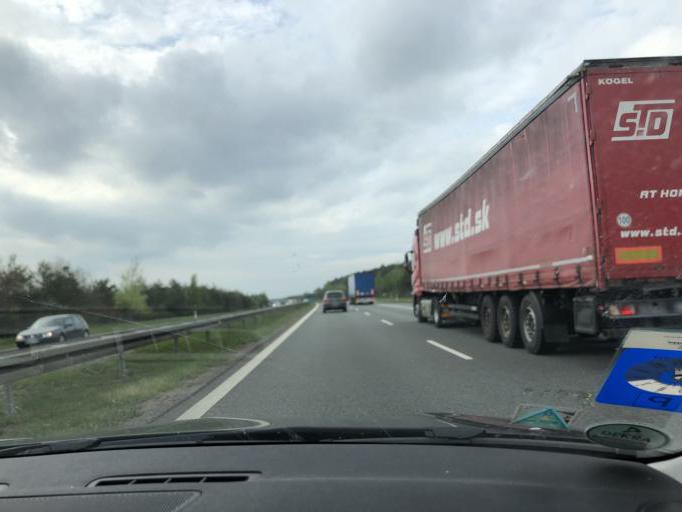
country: PL
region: Opole Voivodeship
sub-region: Powiat opolski
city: Dabrowa
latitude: 50.6471
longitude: 17.7273
